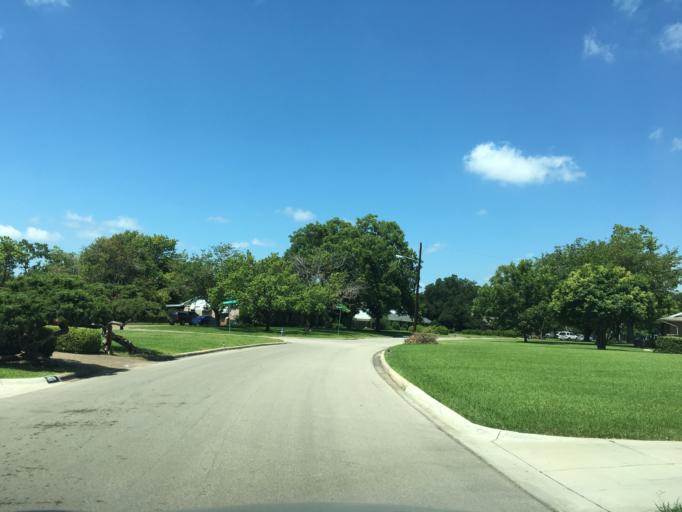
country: US
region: Texas
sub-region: Dallas County
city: Garland
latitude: 32.8368
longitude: -96.6520
